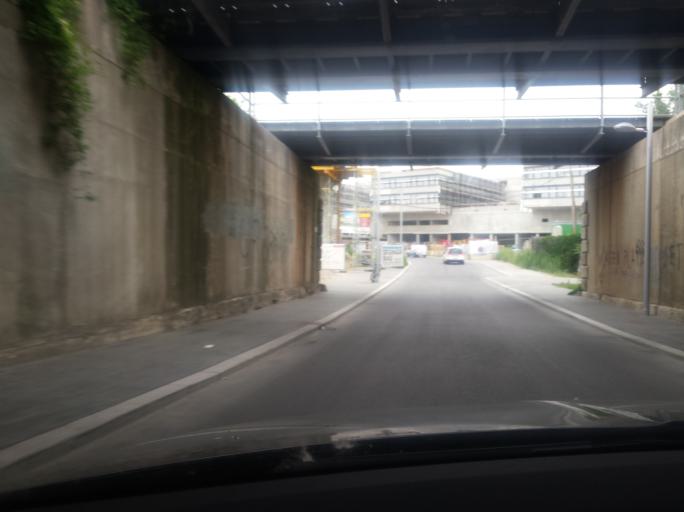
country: AT
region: Vienna
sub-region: Wien Stadt
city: Vienna
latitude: 48.1802
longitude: 16.4244
